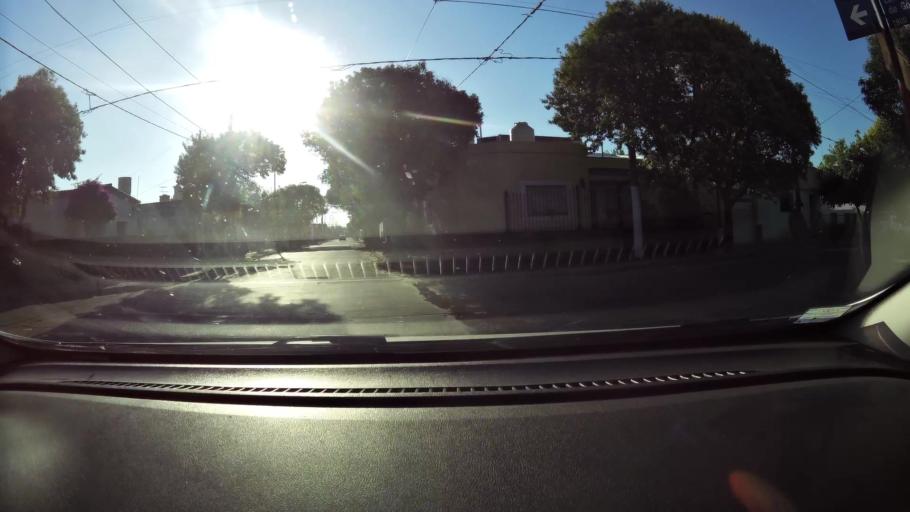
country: AR
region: Cordoba
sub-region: Departamento de Capital
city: Cordoba
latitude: -31.3805
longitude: -64.1983
